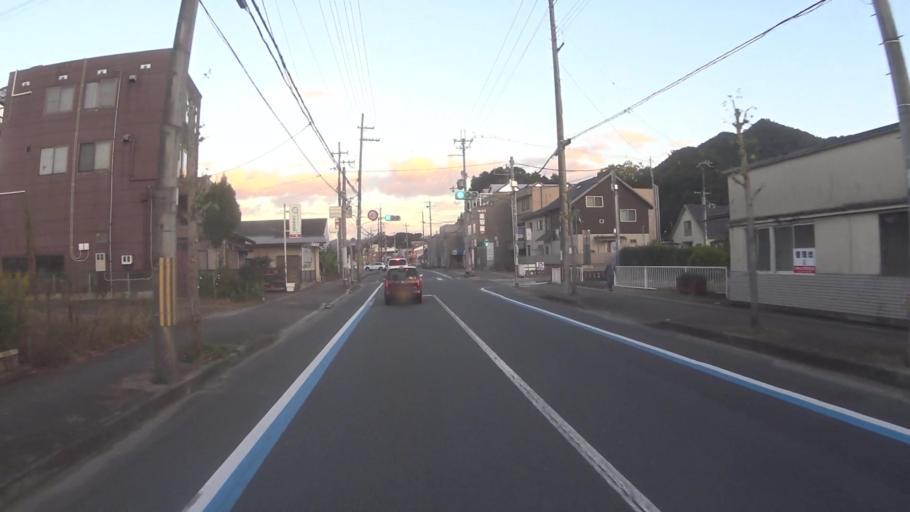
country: JP
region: Kyoto
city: Ayabe
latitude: 35.3025
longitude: 135.2371
